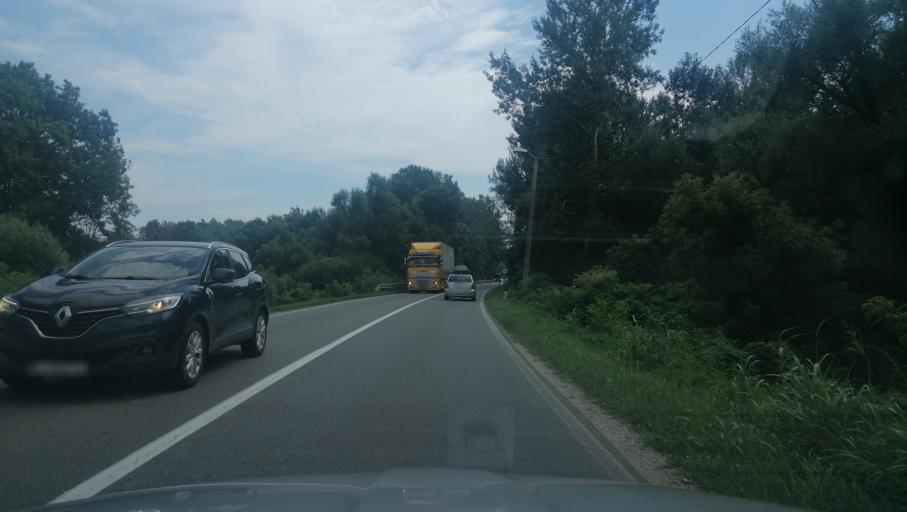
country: BA
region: Brcko
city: Brcko
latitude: 44.9259
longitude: 18.7328
